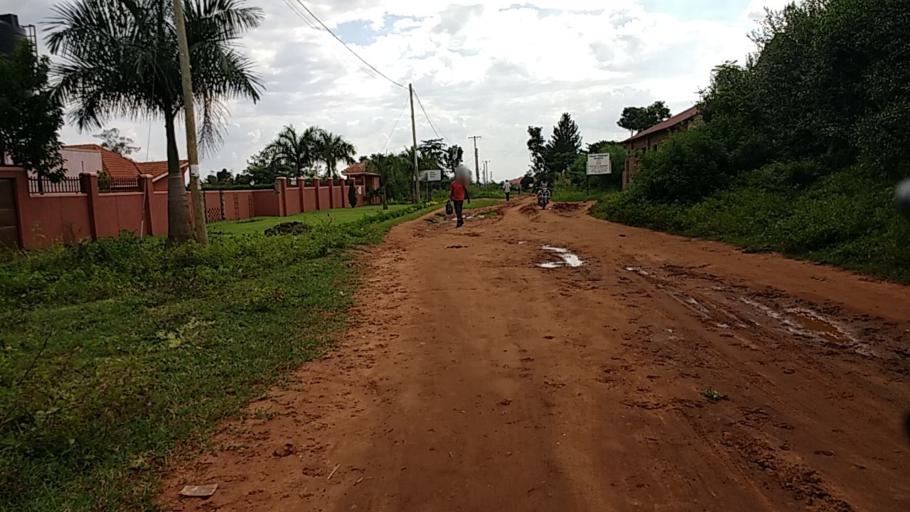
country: UG
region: Eastern Region
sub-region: Mbale District
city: Mbale
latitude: 1.0671
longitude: 34.1671
